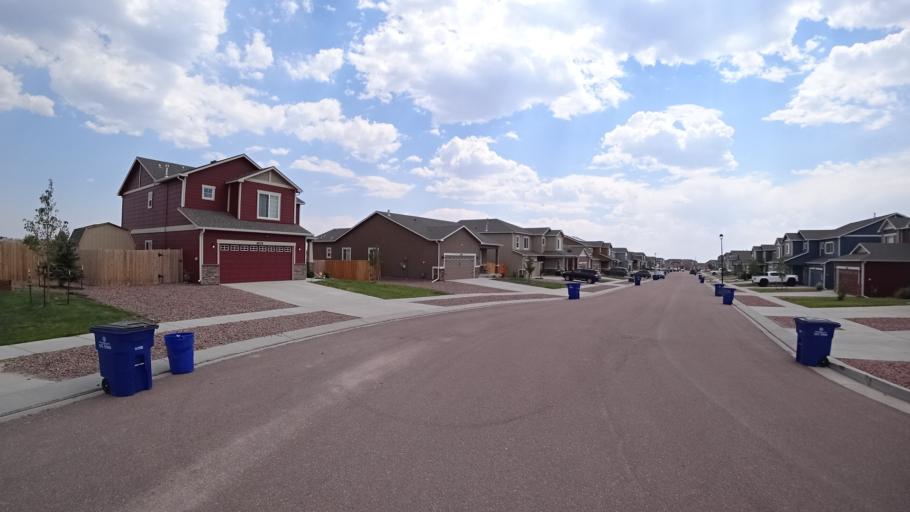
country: US
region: Colorado
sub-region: El Paso County
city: Black Forest
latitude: 38.9475
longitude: -104.6850
